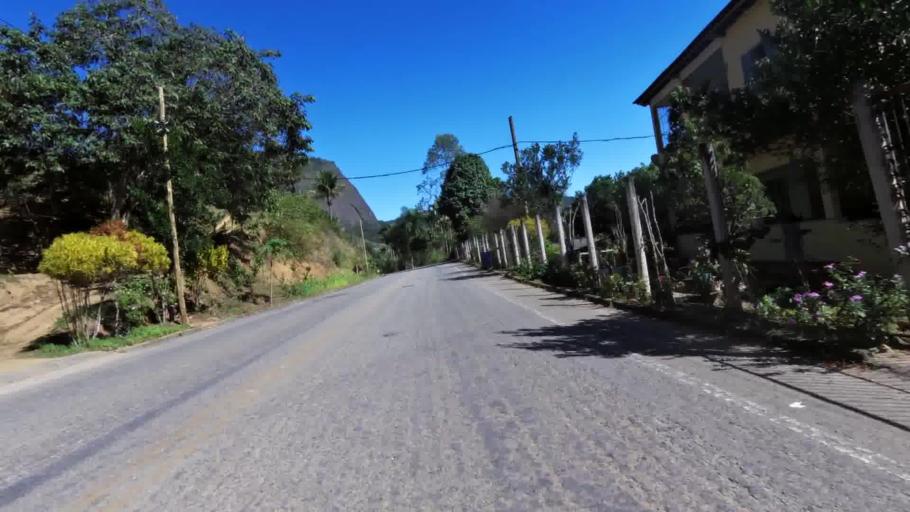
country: BR
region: Espirito Santo
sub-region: Iconha
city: Iconha
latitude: -20.7202
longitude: -40.8976
